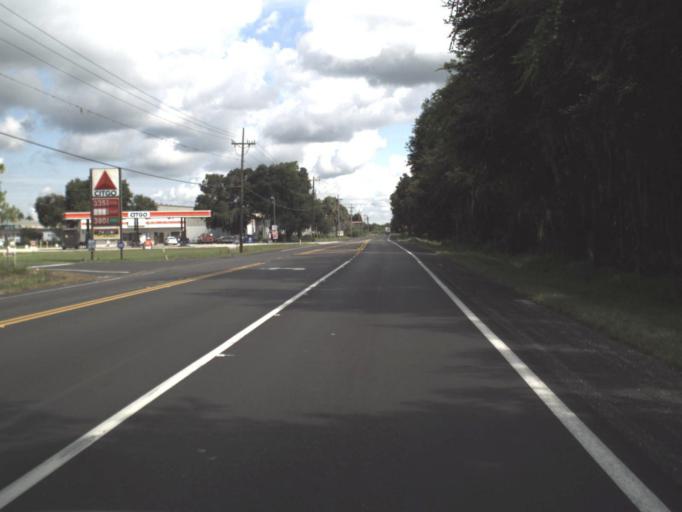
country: US
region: Florida
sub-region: Polk County
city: Combee Settlement
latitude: 28.1008
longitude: -81.9055
